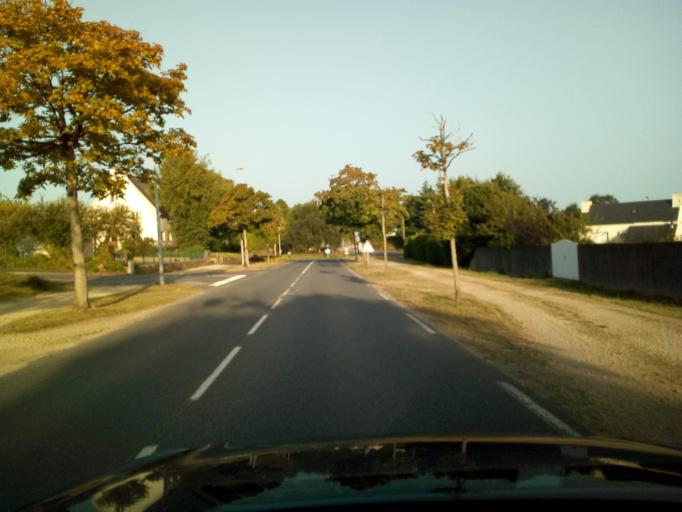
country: FR
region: Brittany
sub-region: Departement du Finistere
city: Landivisiau
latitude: 48.5048
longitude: -4.0751
